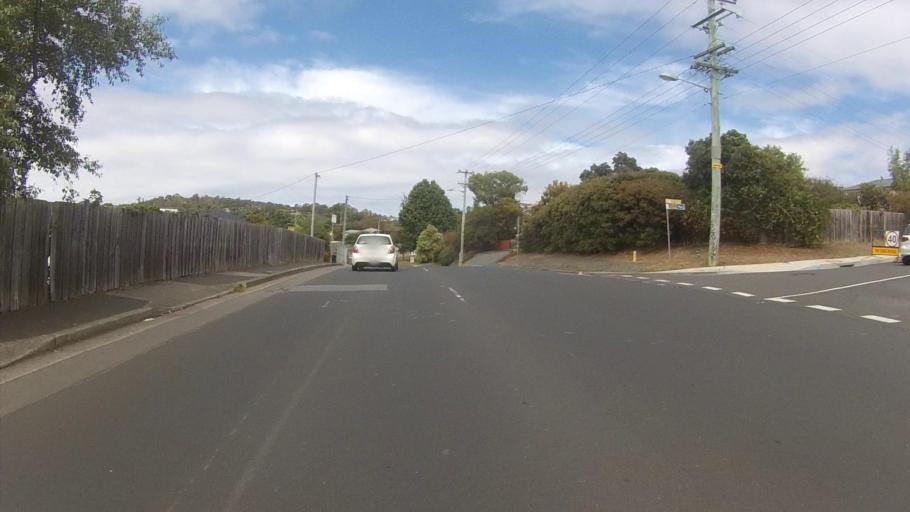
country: AU
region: Tasmania
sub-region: Kingborough
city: Blackmans Bay
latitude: -43.0022
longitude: 147.3193
